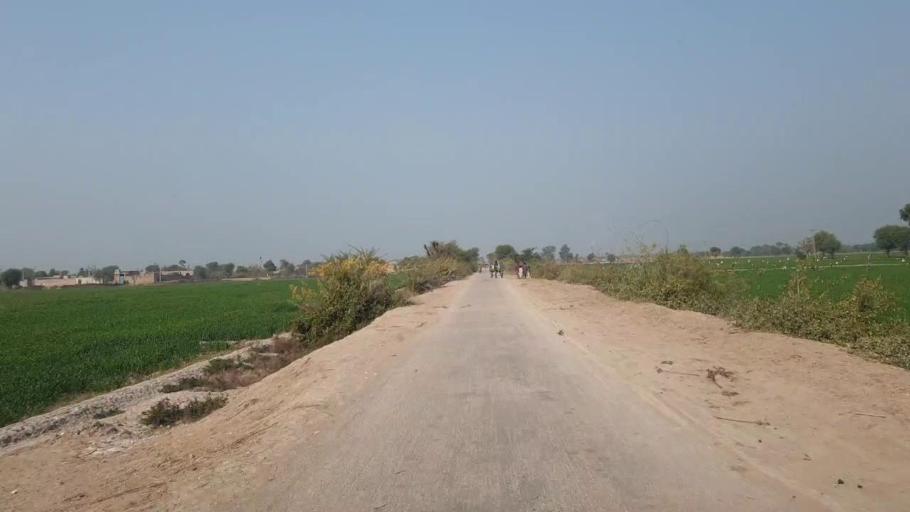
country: PK
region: Sindh
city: Hala
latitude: 25.8529
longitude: 68.4619
